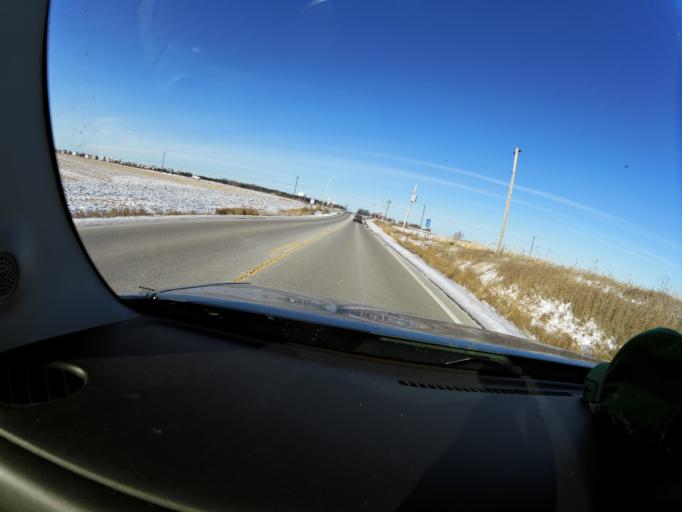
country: US
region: Minnesota
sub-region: Washington County
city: Afton
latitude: 44.8898
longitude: -92.8624
